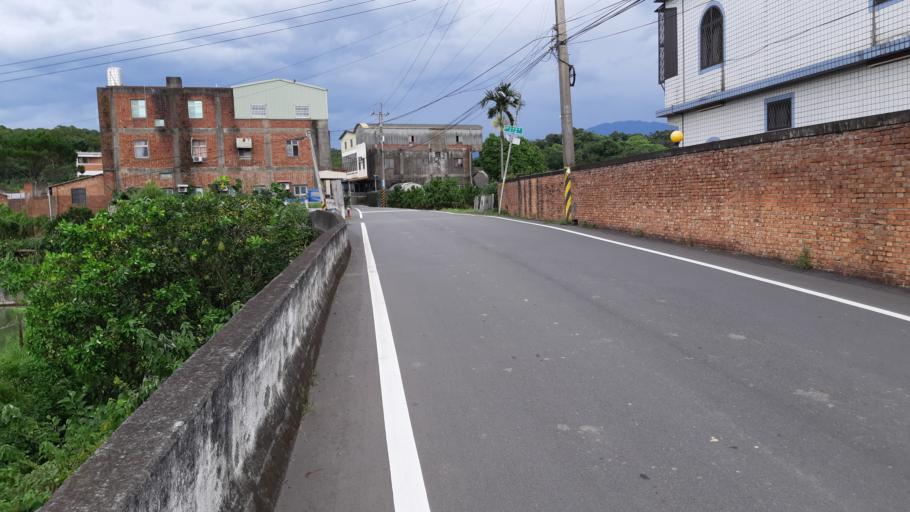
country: TW
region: Taiwan
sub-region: Miaoli
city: Miaoli
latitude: 24.6577
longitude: 120.8883
